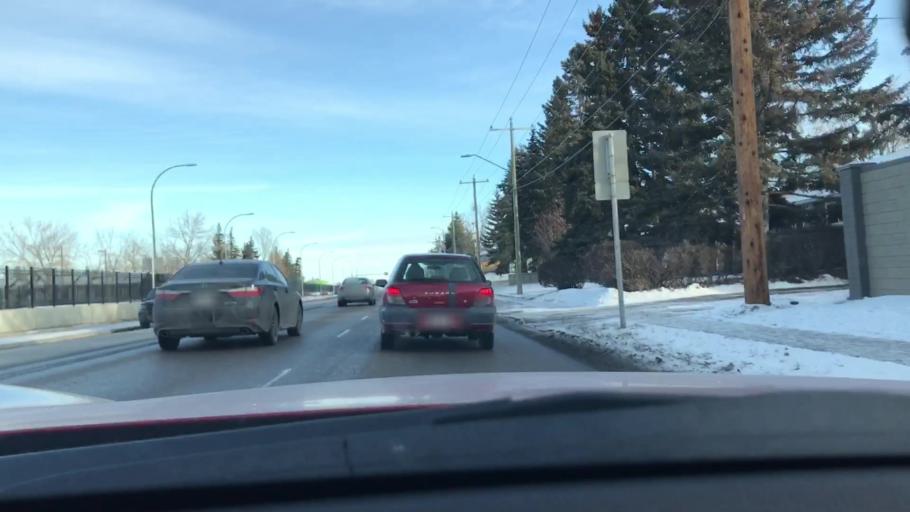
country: CA
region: Alberta
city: Calgary
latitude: 51.0378
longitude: -114.1523
